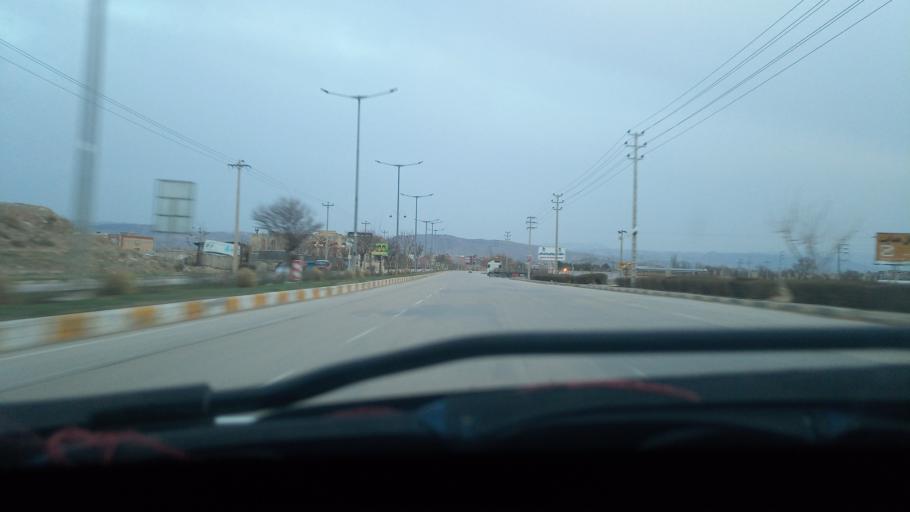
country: IR
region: Khorasan-e Shomali
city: Bojnurd
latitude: 37.4475
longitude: 57.3162
